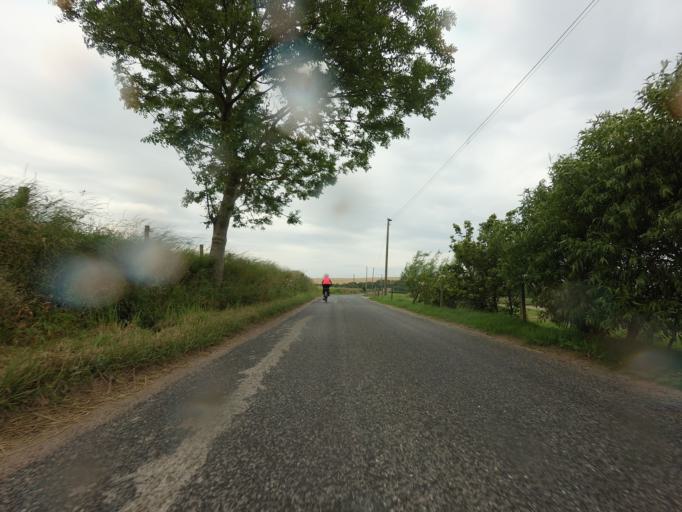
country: GB
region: Scotland
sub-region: Aberdeenshire
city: Portsoy
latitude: 57.6758
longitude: -2.6480
